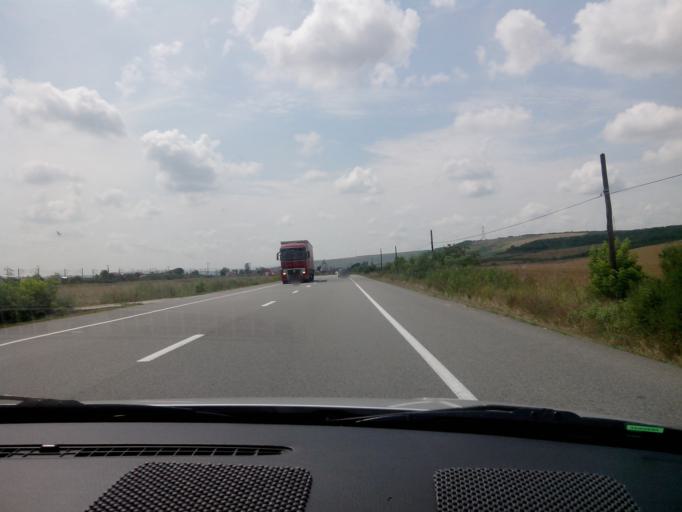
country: RO
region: Cluj
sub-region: Comuna Bontida
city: Rascruci
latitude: 46.9337
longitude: 23.7870
